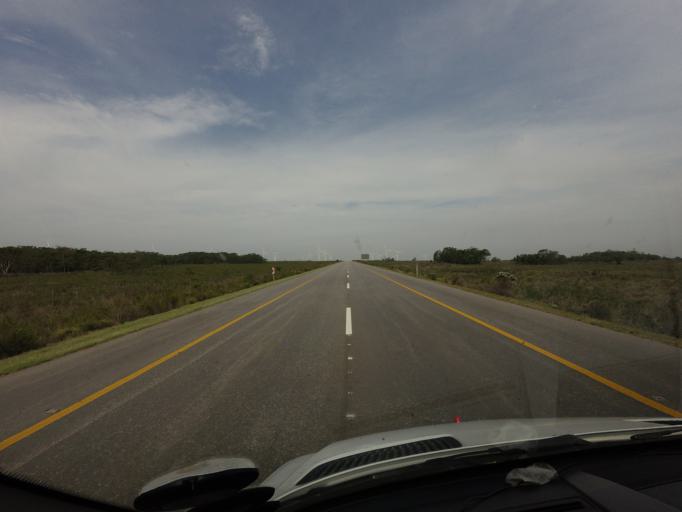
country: ZA
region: Eastern Cape
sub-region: Cacadu District Municipality
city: Kruisfontein
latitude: -34.0117
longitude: 24.7966
